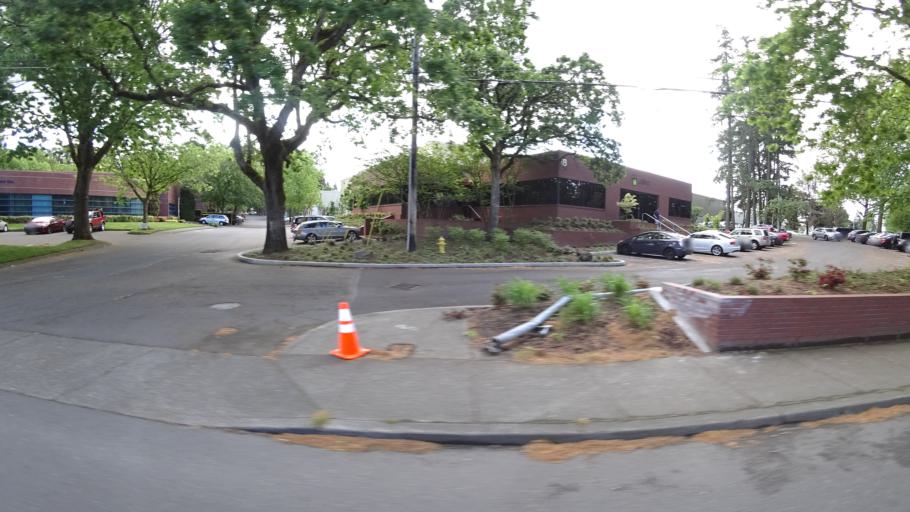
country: US
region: Oregon
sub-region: Washington County
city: Durham
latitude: 45.4041
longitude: -122.7493
